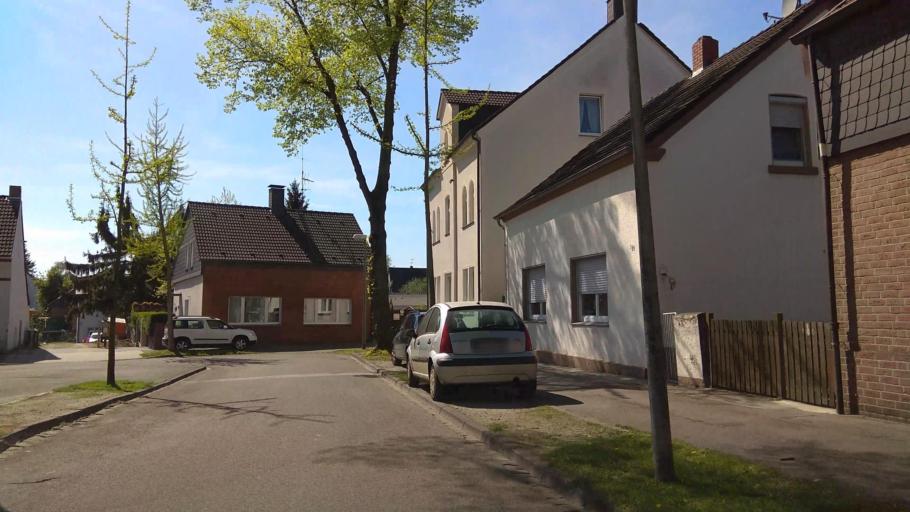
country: DE
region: North Rhine-Westphalia
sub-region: Regierungsbezirk Munster
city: Gelsenkirchen
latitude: 51.5646
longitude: 7.0795
